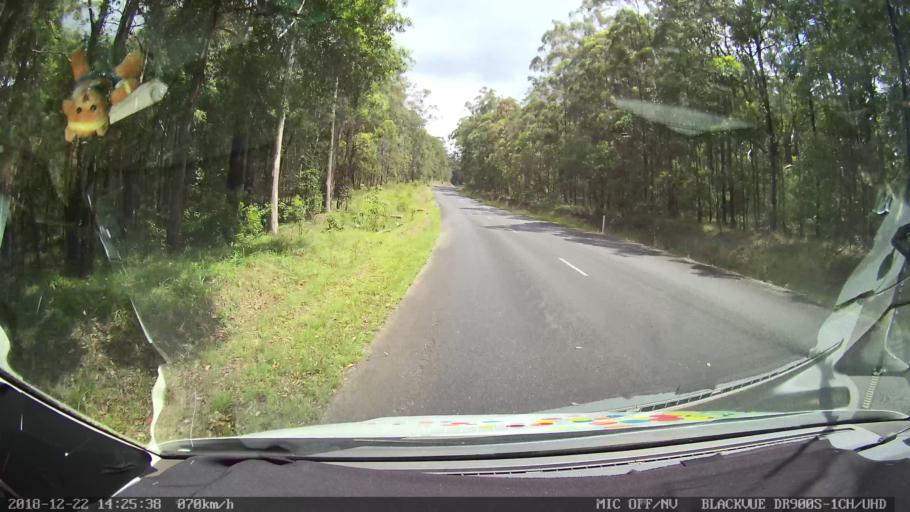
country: AU
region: New South Wales
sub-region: Bellingen
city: Dorrigo
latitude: -30.0521
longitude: 152.6373
